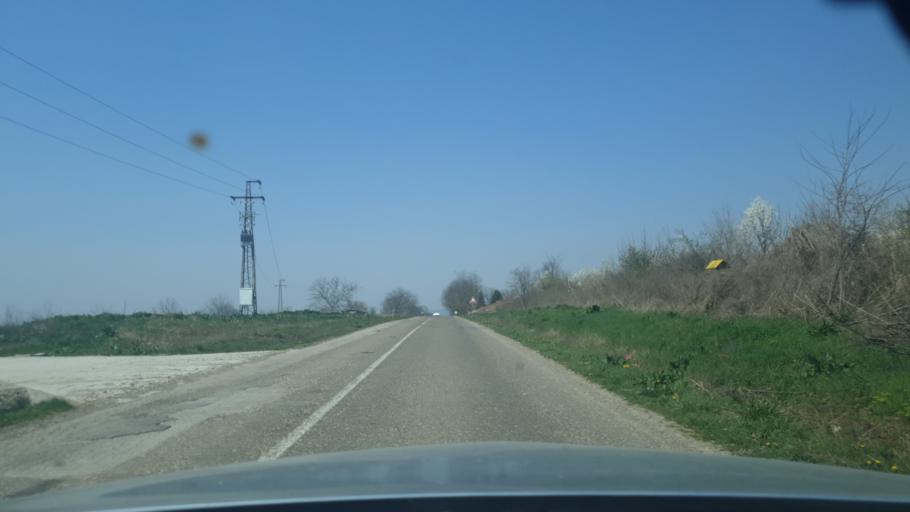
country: RS
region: Autonomna Pokrajina Vojvodina
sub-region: Sremski Okrug
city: Ruma
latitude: 45.0109
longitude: 19.7839
